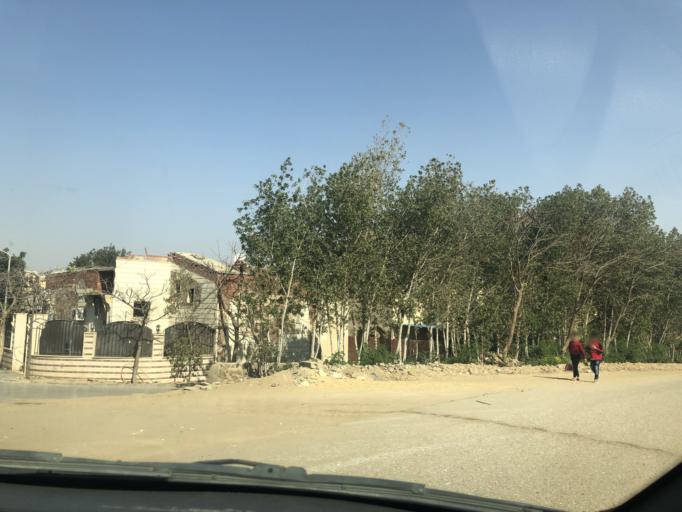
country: EG
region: Al Jizah
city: Madinat Sittah Uktubar
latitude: 29.9547
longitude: 31.0072
